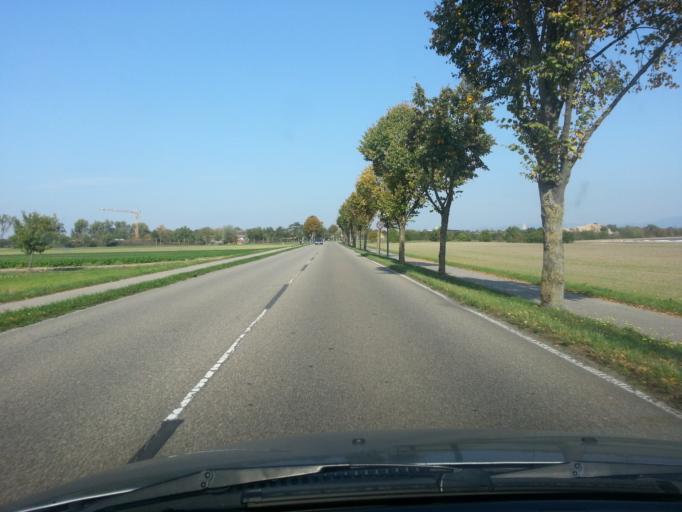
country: DE
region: Baden-Wuerttemberg
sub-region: Karlsruhe Region
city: Neulussheim
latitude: 49.3014
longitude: 8.5263
